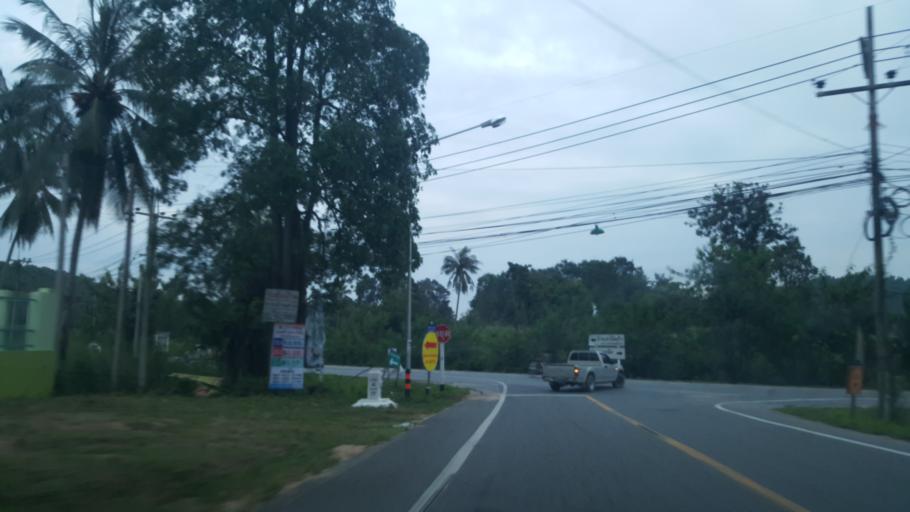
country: TH
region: Chon Buri
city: Ban Talat Bueng
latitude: 12.9597
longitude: 101.0138
